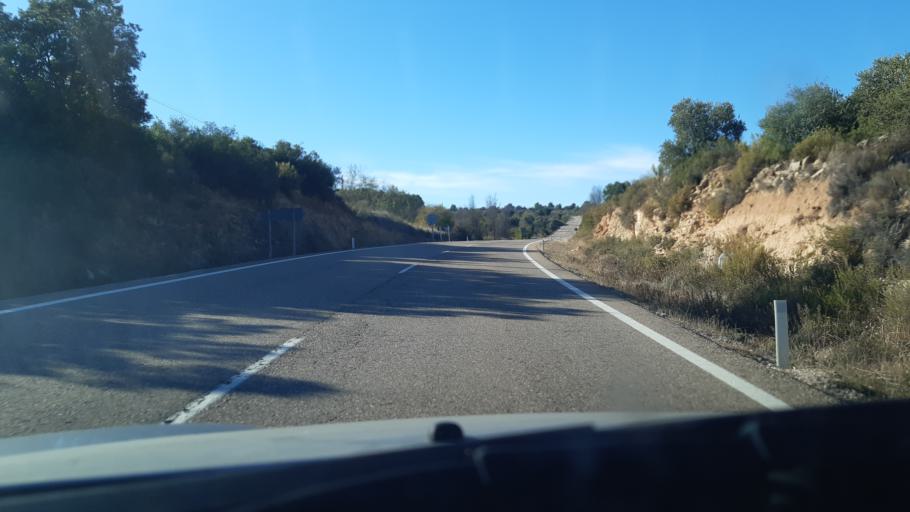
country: ES
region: Aragon
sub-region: Provincia de Teruel
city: Valjunquera
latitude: 40.9598
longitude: -0.0058
